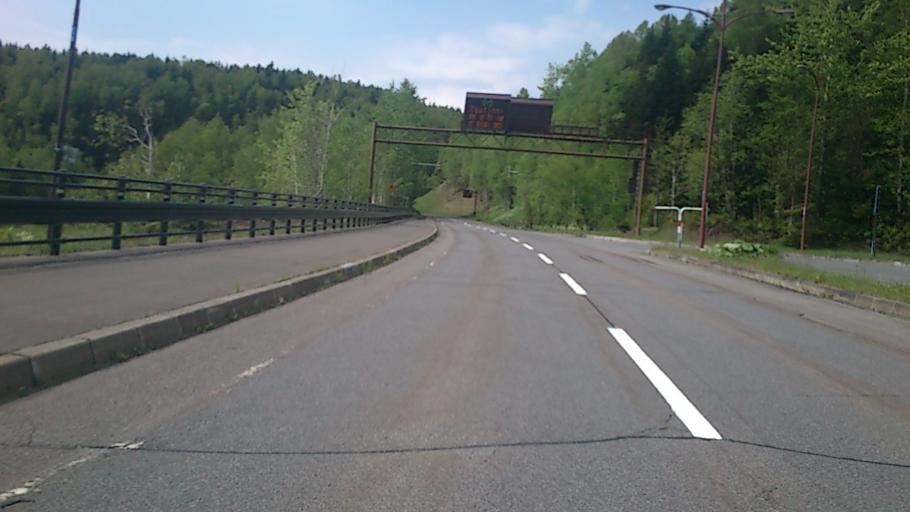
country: JP
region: Hokkaido
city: Kamikawa
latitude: 43.6652
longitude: 143.0362
